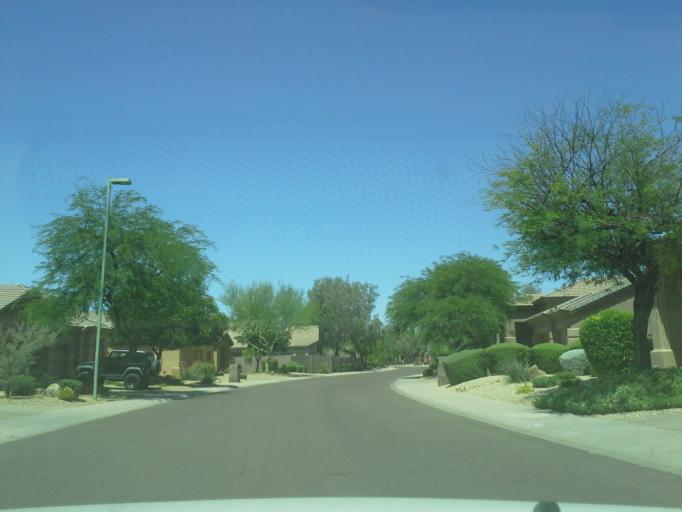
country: US
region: Arizona
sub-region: Maricopa County
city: Paradise Valley
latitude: 33.6171
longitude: -111.9397
